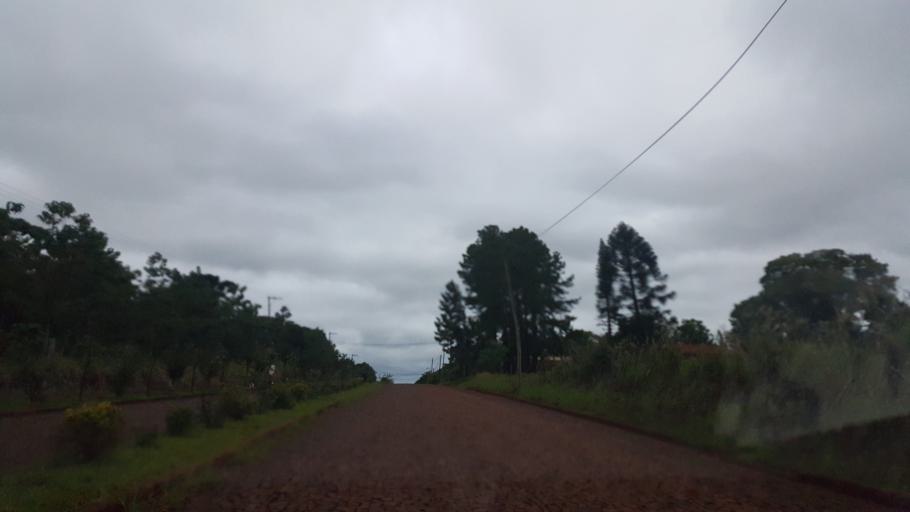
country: AR
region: Misiones
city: Ruiz de Montoya
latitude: -26.9642
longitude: -55.0569
